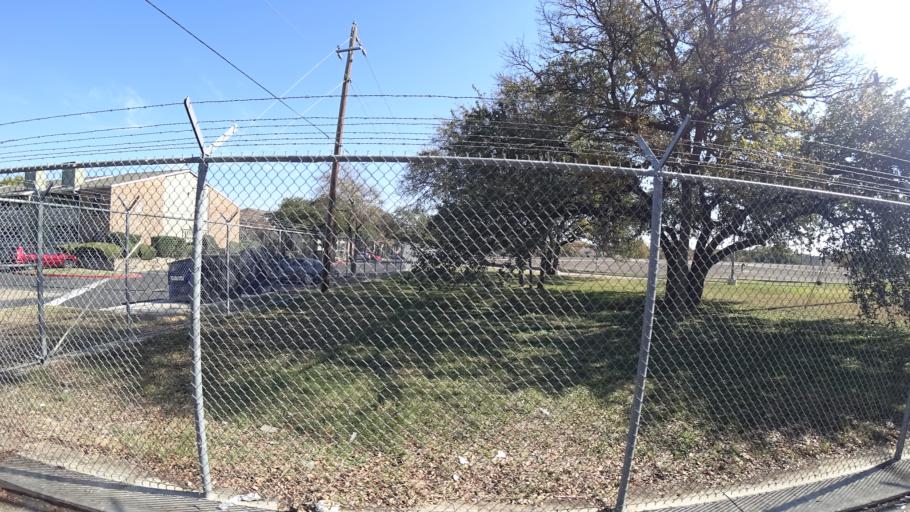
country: US
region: Texas
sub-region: Williamson County
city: Jollyville
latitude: 30.3728
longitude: -97.7553
